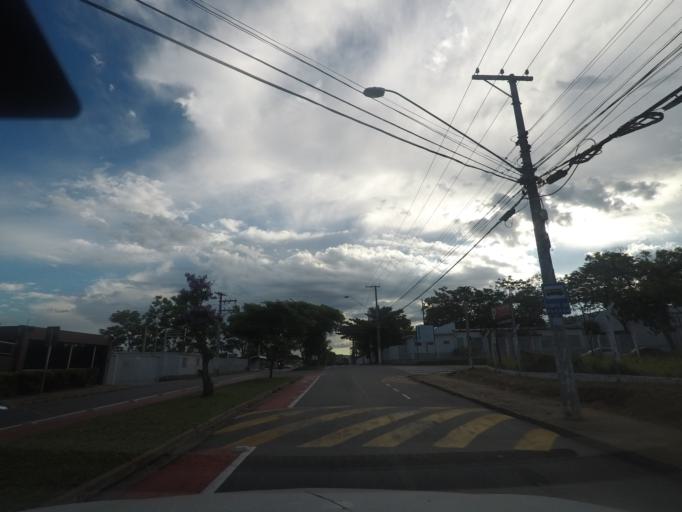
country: BR
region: Sao Paulo
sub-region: Taubate
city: Taubate
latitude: -23.0477
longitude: -45.5974
